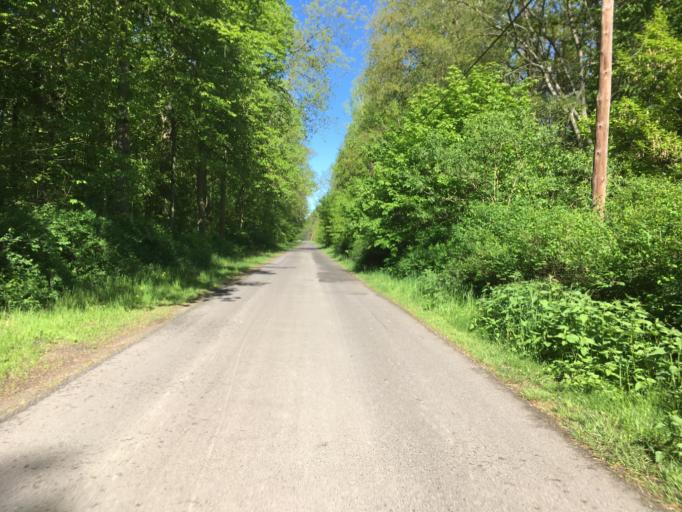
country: DE
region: Brandenburg
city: Liebenwalde
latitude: 52.9450
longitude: 13.4656
